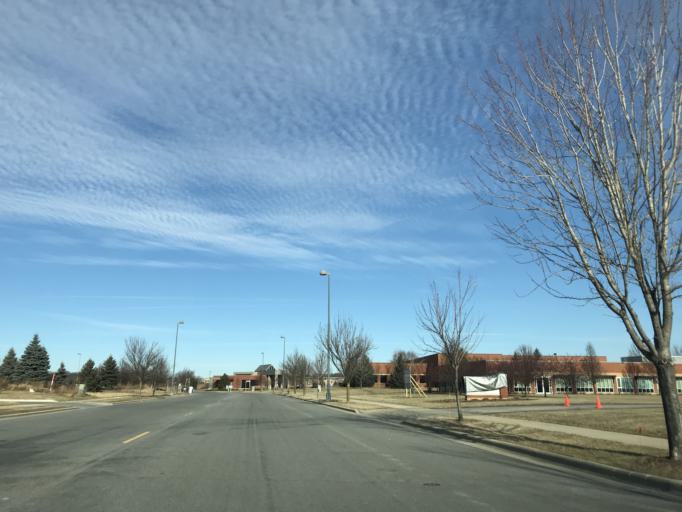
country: US
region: Wisconsin
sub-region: Dane County
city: Windsor
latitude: 43.1491
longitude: -89.2938
